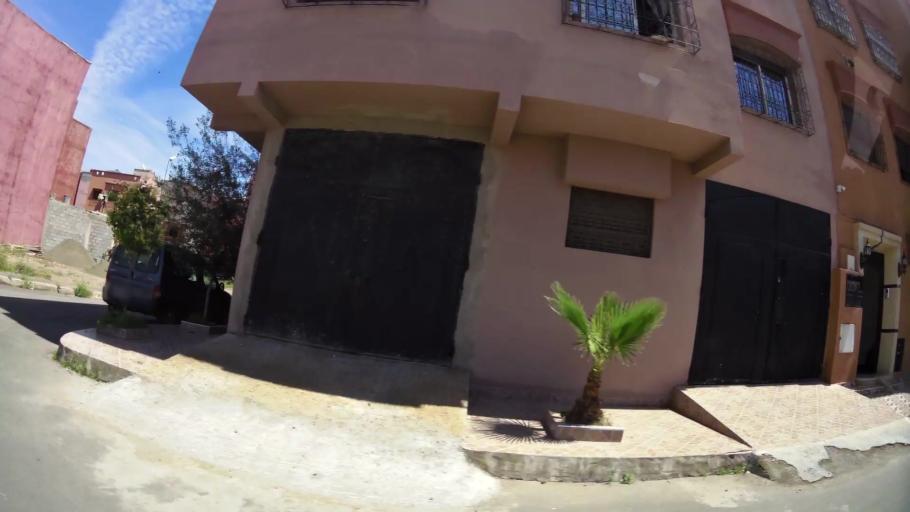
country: MA
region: Marrakech-Tensift-Al Haouz
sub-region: Marrakech
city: Marrakesh
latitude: 31.6370
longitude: -8.0494
